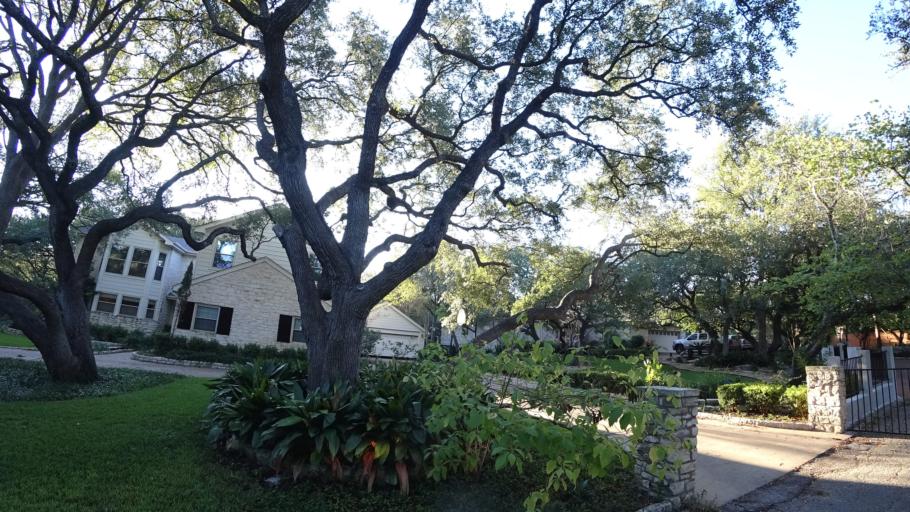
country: US
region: Texas
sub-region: Travis County
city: West Lake Hills
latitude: 30.3425
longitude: -97.8107
